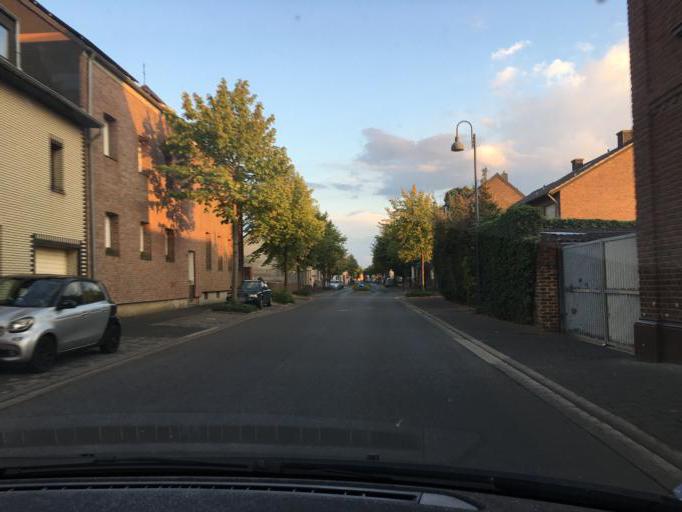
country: DE
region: North Rhine-Westphalia
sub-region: Regierungsbezirk Koln
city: Niederzier
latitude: 50.8562
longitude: 6.4574
